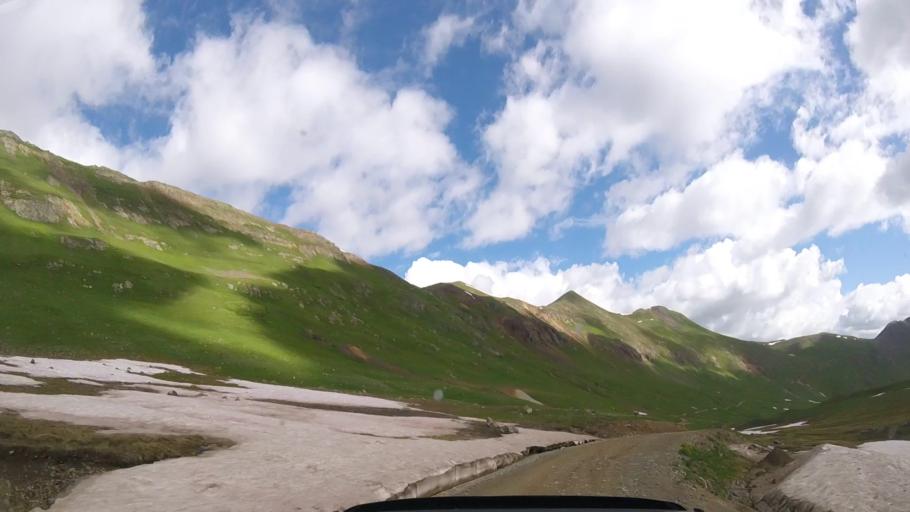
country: US
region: Colorado
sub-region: San Juan County
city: Silverton
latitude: 37.9187
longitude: -107.6130
